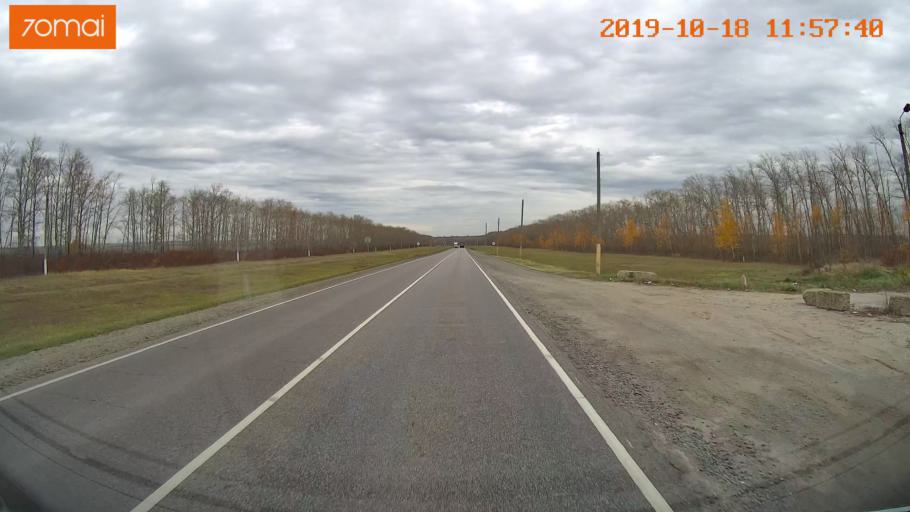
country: RU
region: Rjazan
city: Mikhaylov
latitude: 54.2668
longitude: 39.1498
